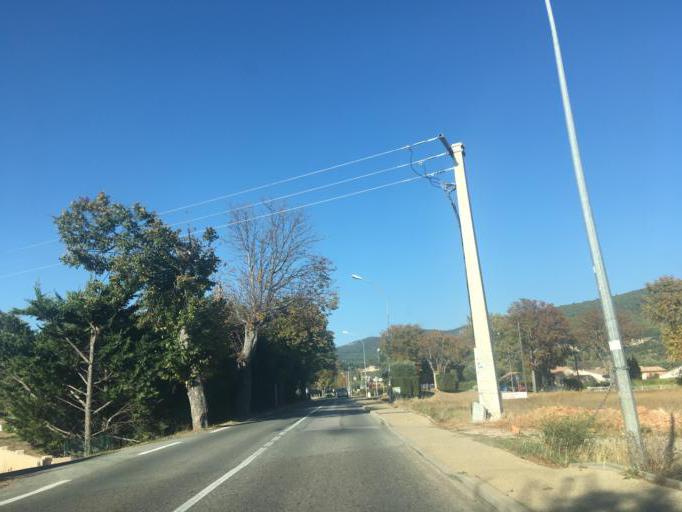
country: FR
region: Provence-Alpes-Cote d'Azur
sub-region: Departement du Var
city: Aups
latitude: 43.6194
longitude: 6.2210
